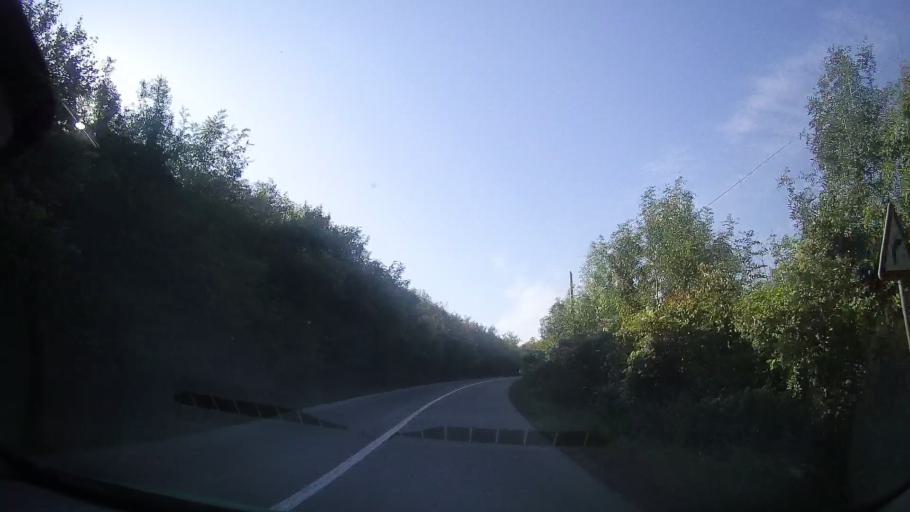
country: RO
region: Timis
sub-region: Oras Recas
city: Recas
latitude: 45.8369
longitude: 21.5217
